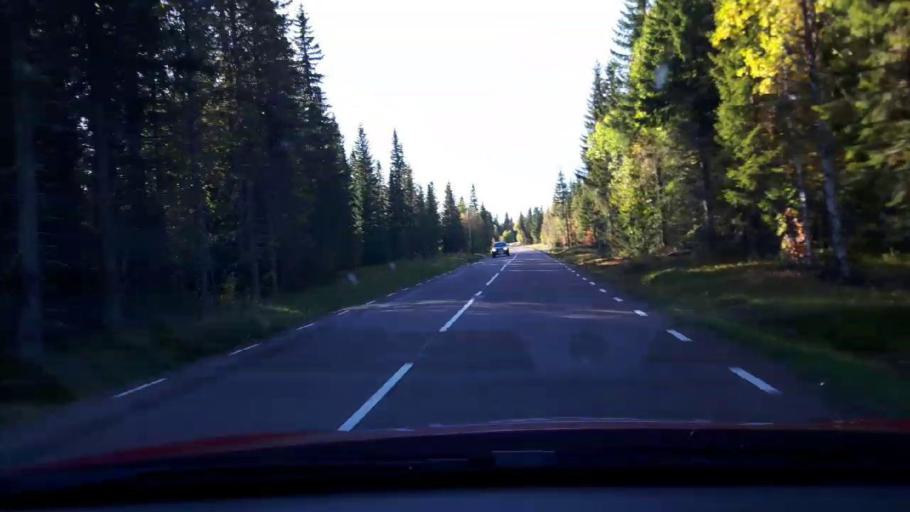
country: SE
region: Jaemtland
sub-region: Stroemsunds Kommun
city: Stroemsund
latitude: 63.8649
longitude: 15.1448
